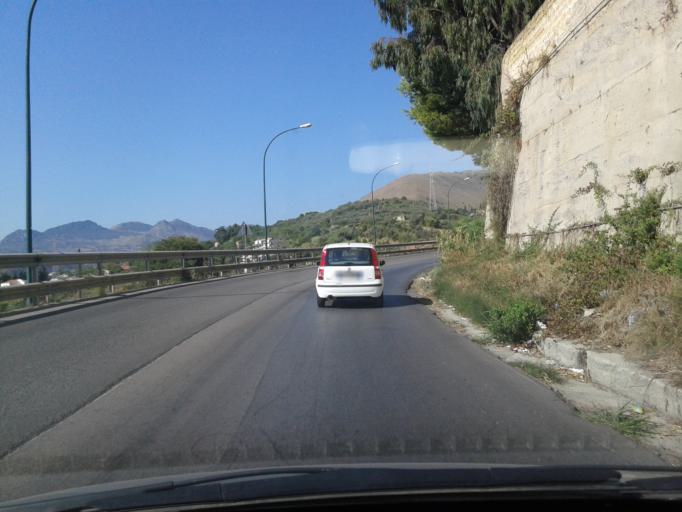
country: IT
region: Sicily
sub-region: Palermo
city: Monreale
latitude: 38.0746
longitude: 13.2868
